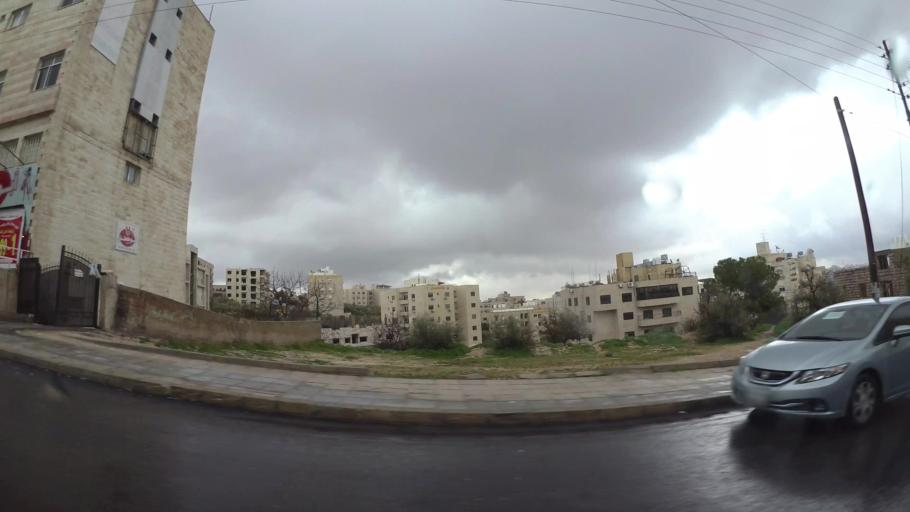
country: JO
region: Amman
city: Al Jubayhah
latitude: 32.0209
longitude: 35.8661
